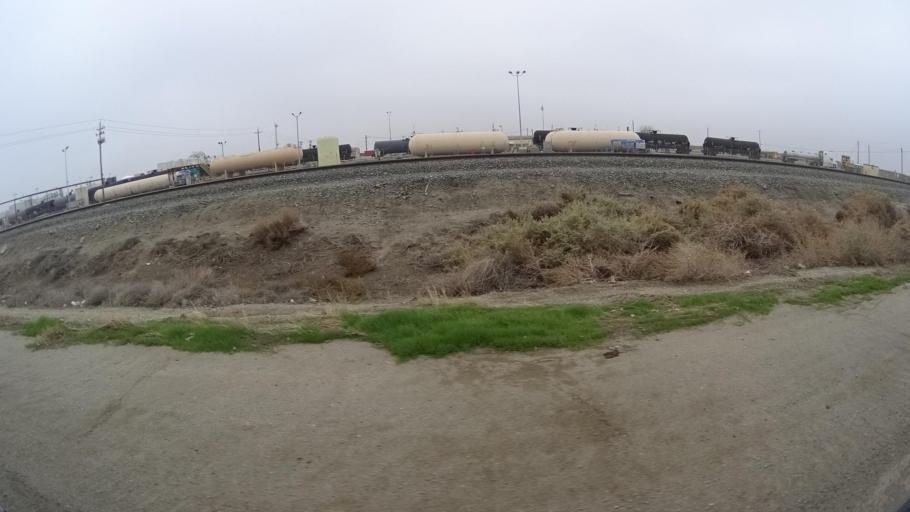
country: US
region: California
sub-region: Kern County
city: Greenfield
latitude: 35.1802
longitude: -119.1623
